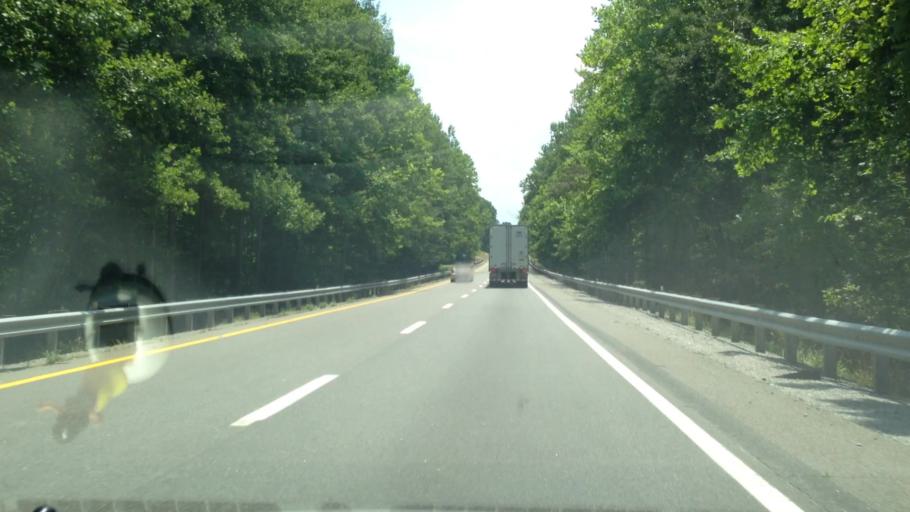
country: US
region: Virginia
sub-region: City of Martinsville
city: Martinsville
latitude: 36.6345
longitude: -79.8889
